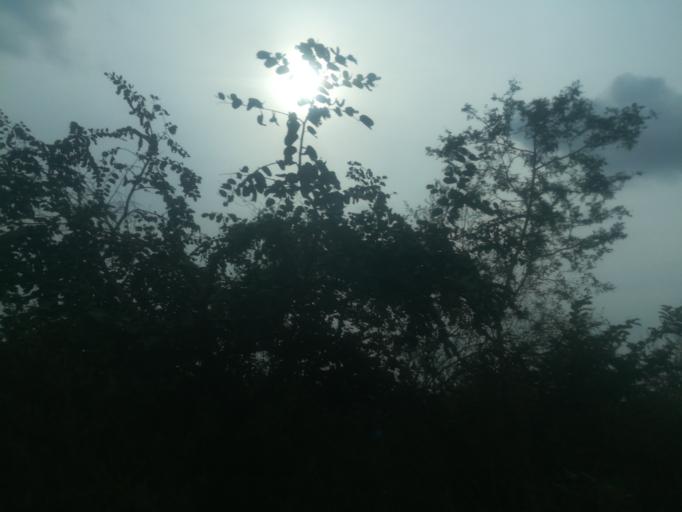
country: NG
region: Ogun
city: Ayetoro
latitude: 7.2969
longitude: 3.0773
